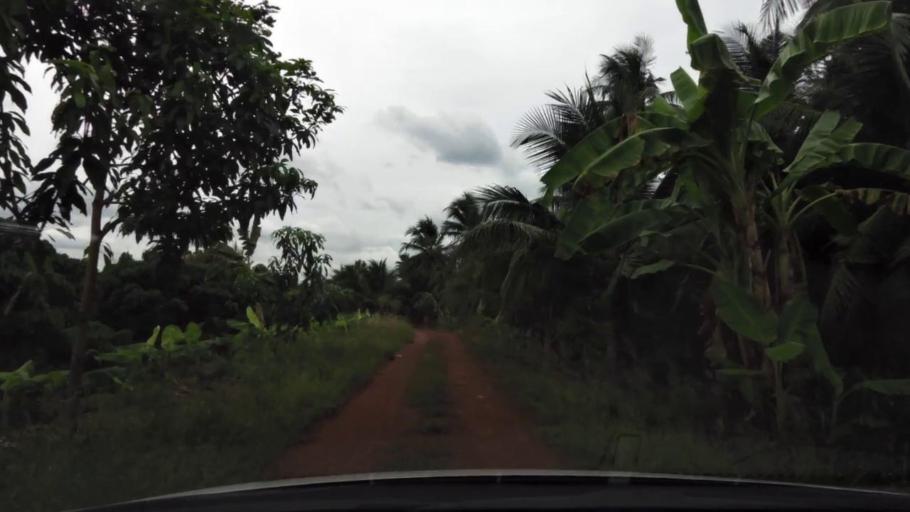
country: TH
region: Ratchaburi
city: Damnoen Saduak
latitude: 13.5562
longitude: 100.0248
